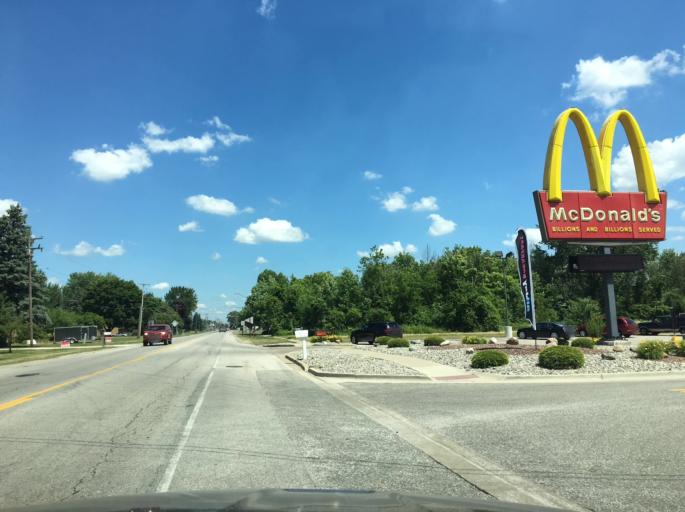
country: US
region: Michigan
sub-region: Bay County
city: Auburn
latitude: 43.5991
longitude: -84.0895
